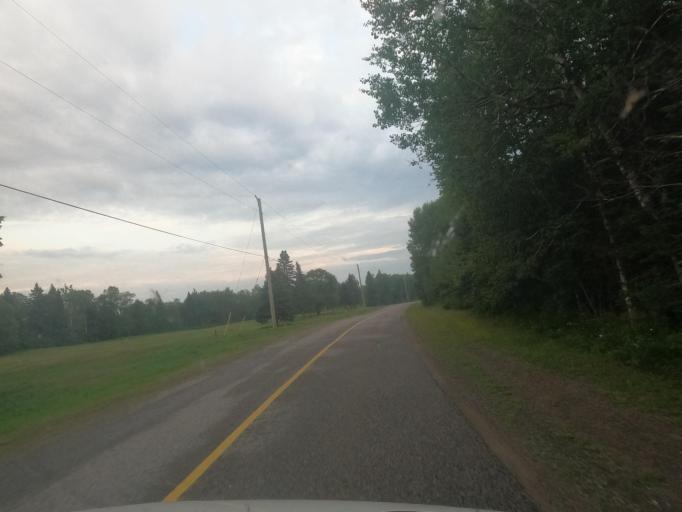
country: CA
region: Ontario
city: Marathon
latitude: 48.7760
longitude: -87.1101
